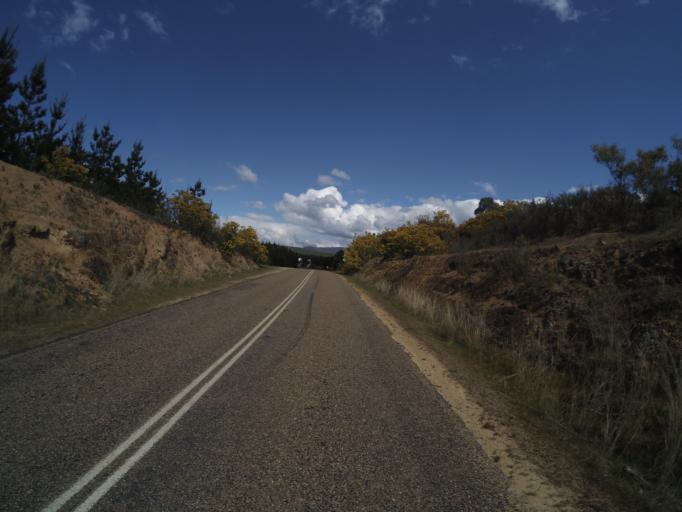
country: AU
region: Australian Capital Territory
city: Macquarie
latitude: -35.3348
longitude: 148.9307
